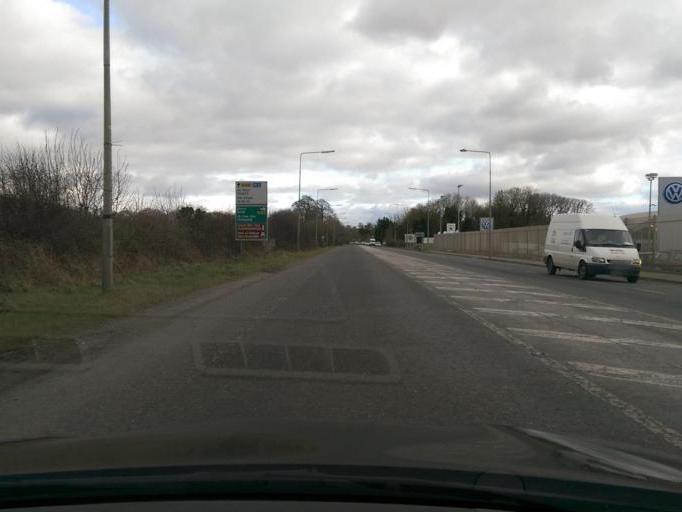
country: IE
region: Leinster
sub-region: An Iarmhi
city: Athlone
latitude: 53.4049
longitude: -7.8841
